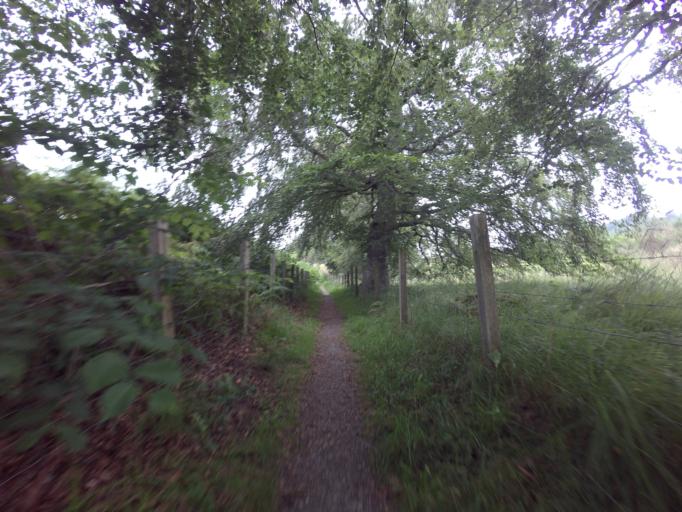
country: GB
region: Scotland
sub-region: Highland
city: Evanton
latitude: 57.9232
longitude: -4.4028
